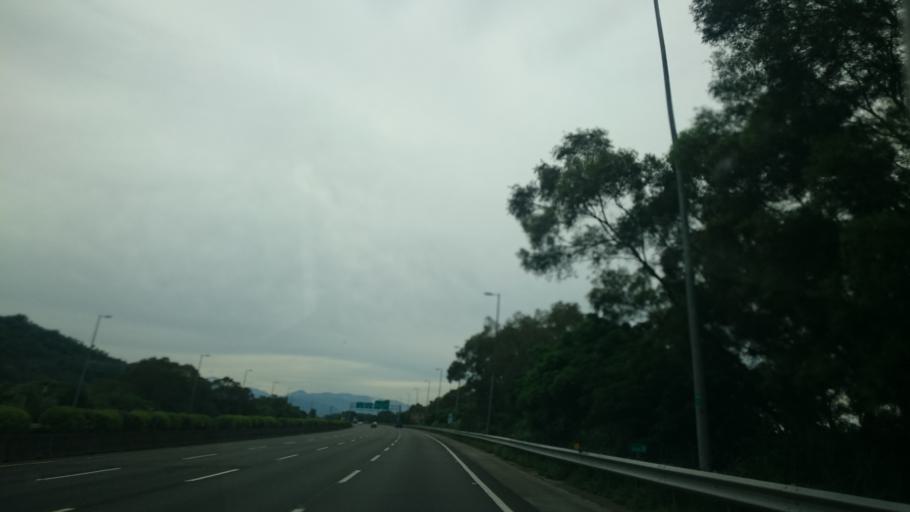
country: TW
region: Taiwan
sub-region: Nantou
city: Nantou
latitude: 23.8591
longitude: 120.7018
